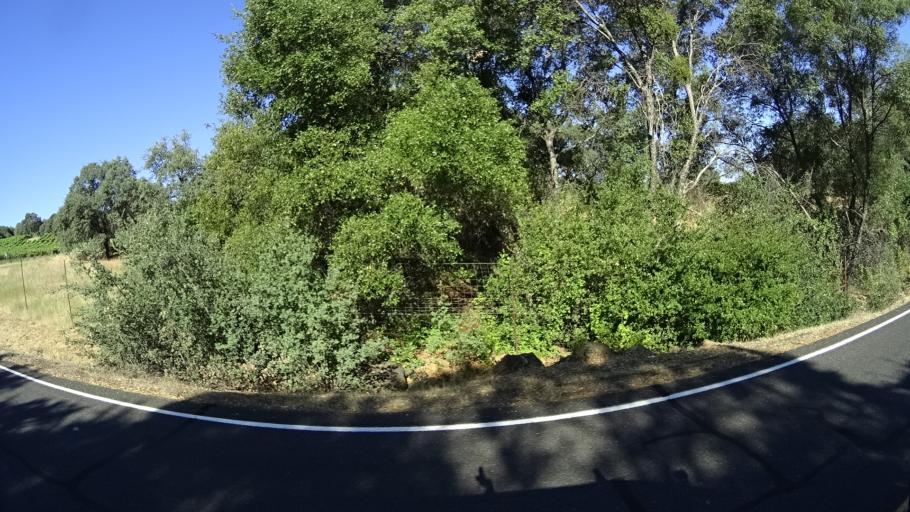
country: US
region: California
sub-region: Calaveras County
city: Murphys
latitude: 38.0906
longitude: -120.4850
